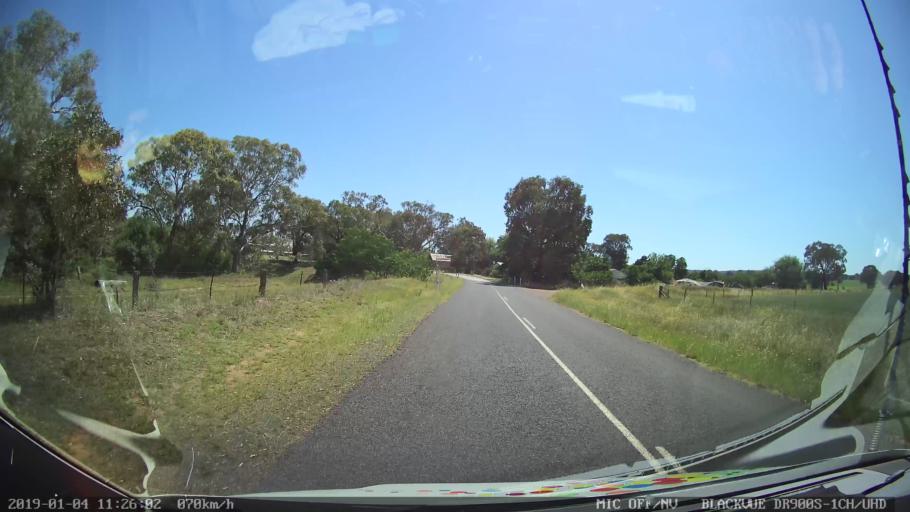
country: AU
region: New South Wales
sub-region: Cabonne
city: Molong
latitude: -33.1181
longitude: 148.7548
